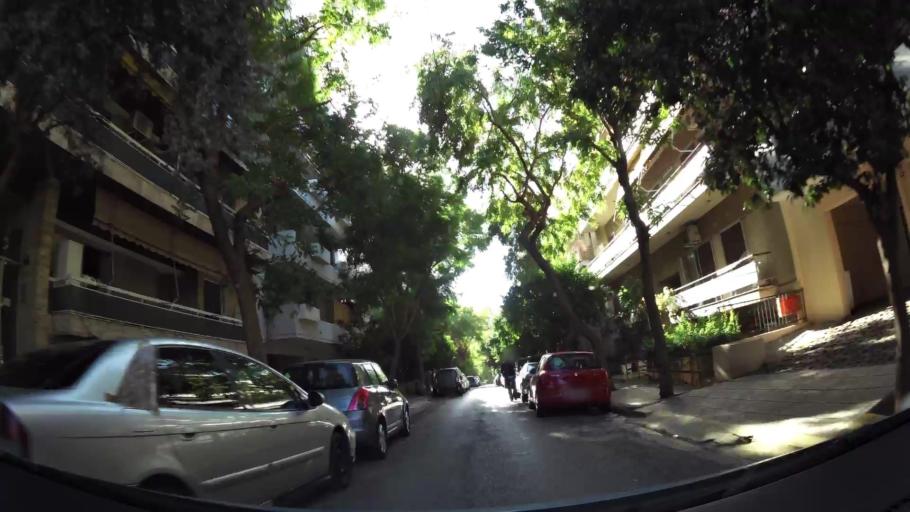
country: GR
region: Attica
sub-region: Nomarchia Athinas
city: Neo Psychiko
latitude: 37.9927
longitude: 23.7711
